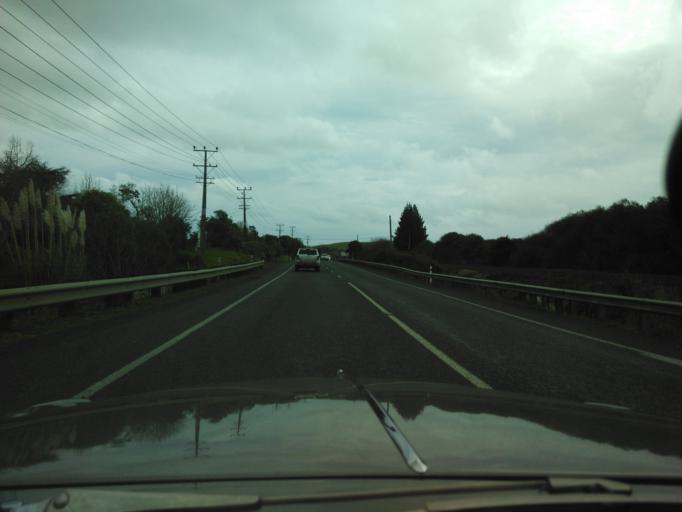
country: NZ
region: Auckland
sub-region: Auckland
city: Muriwai Beach
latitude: -36.7664
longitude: 174.5034
